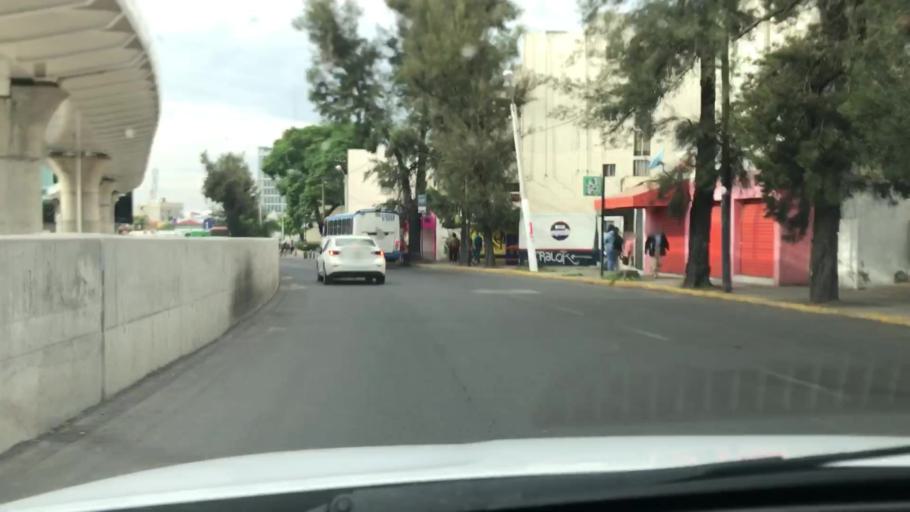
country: MX
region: Jalisco
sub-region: Zapopan
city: Zapopan
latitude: 20.7226
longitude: -103.3878
